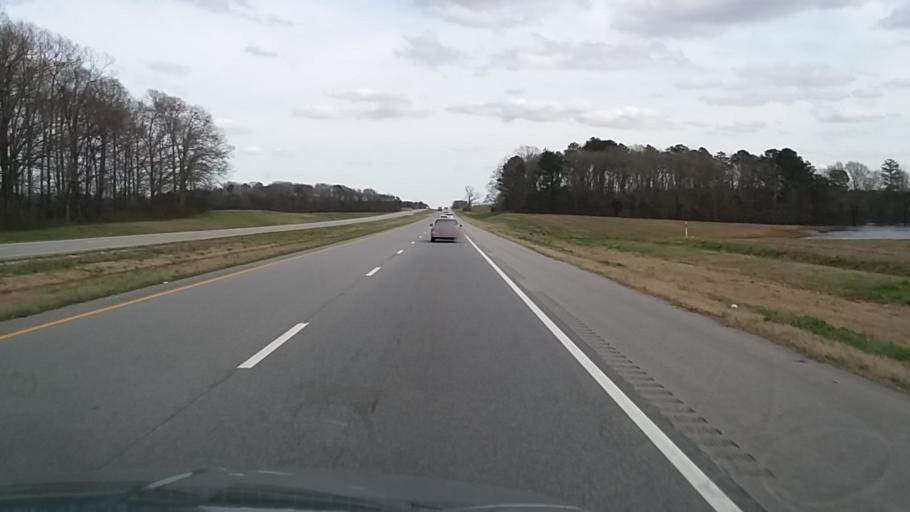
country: US
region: Alabama
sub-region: Lawrence County
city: Town Creek
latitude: 34.6828
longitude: -87.4843
